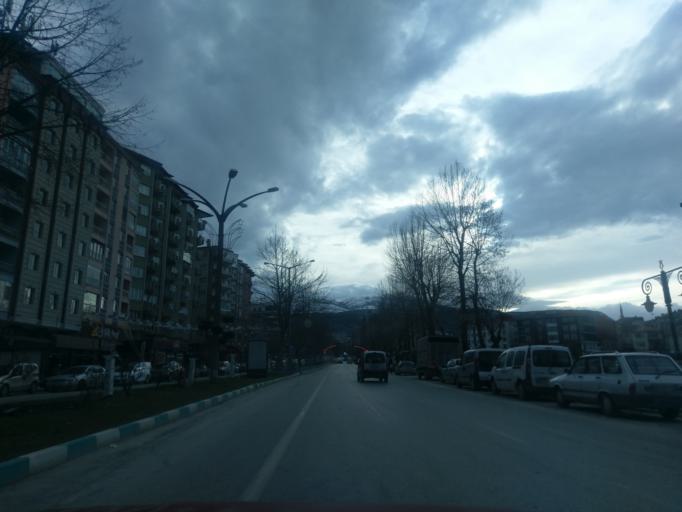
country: TR
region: Kuetahya
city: Kutahya
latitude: 39.4256
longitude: 29.9907
